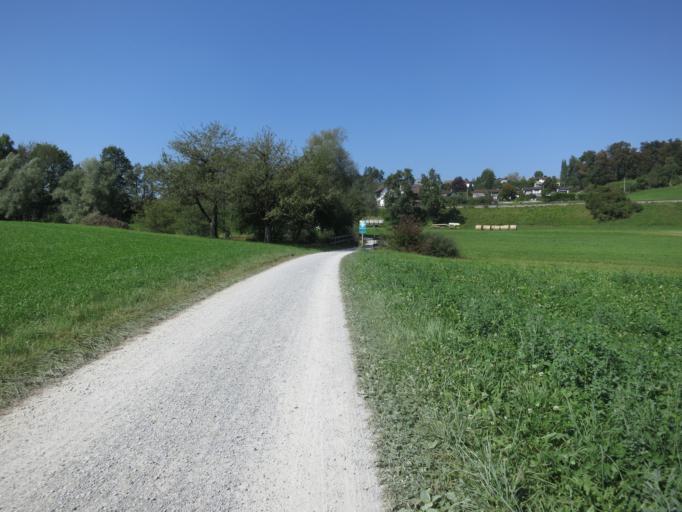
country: CH
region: Zurich
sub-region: Bezirk Hinwil
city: Bubikon
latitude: 47.2614
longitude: 8.8192
